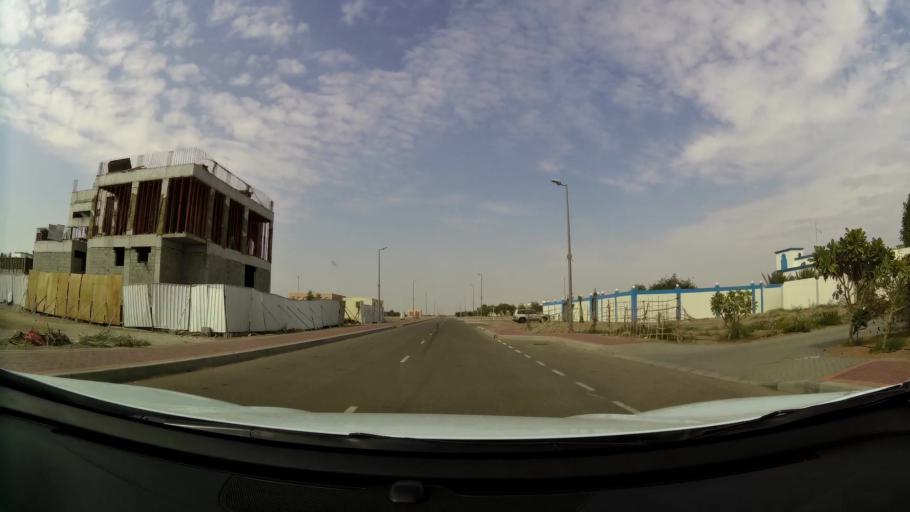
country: AE
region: Abu Dhabi
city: Al Ain
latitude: 24.0969
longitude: 55.8960
